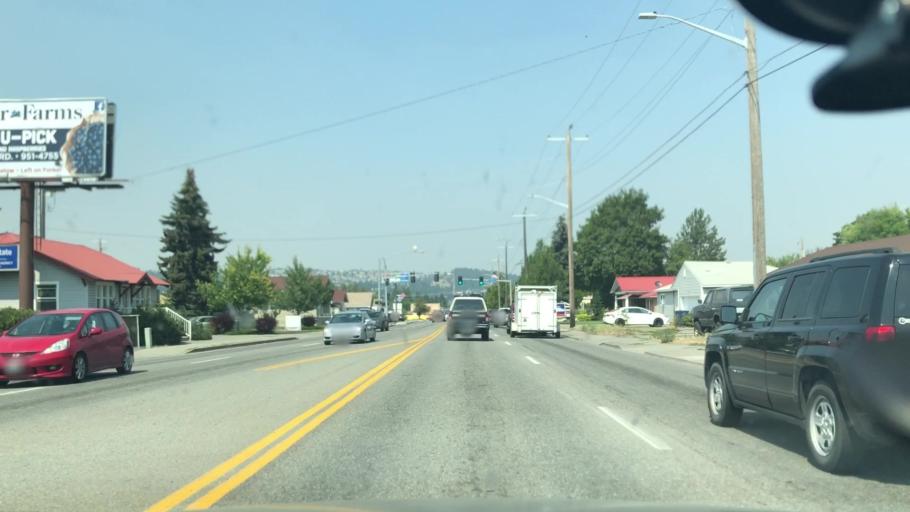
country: US
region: Washington
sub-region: Spokane County
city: Millwood
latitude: 47.6827
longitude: -117.2827
